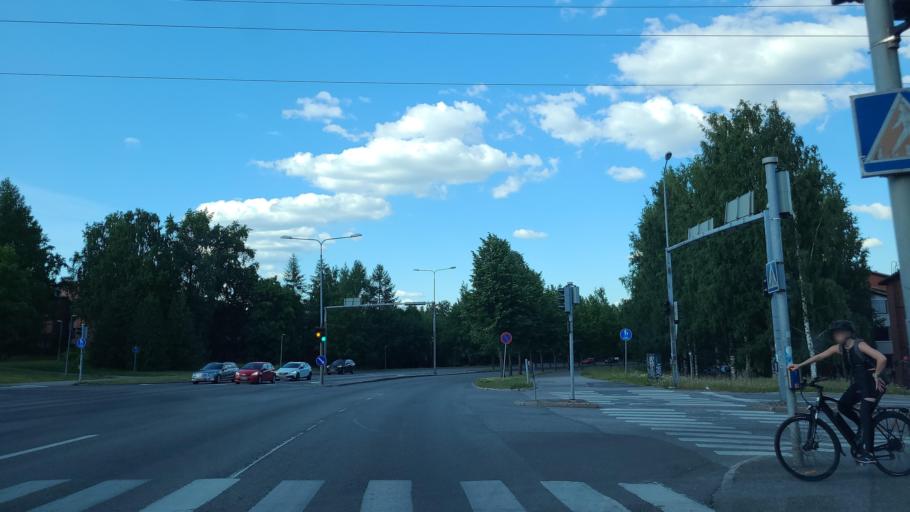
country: FI
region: Central Finland
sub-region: Jyvaeskylae
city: Jyvaeskylae
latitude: 62.2544
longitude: 25.7507
